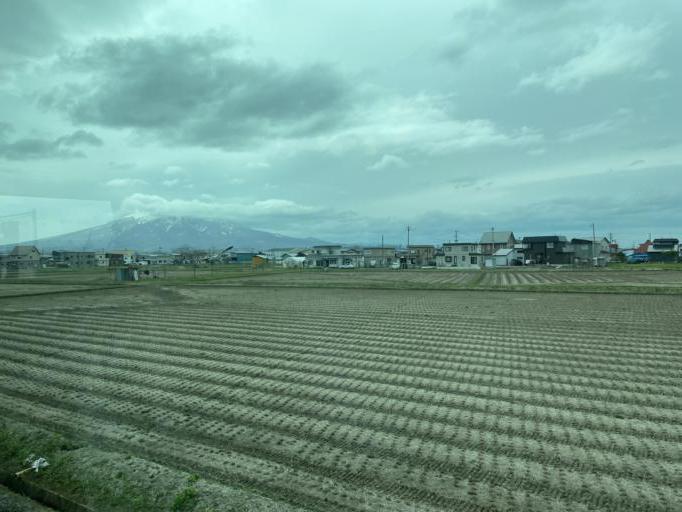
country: JP
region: Aomori
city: Goshogawara
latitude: 40.7524
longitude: 140.4343
